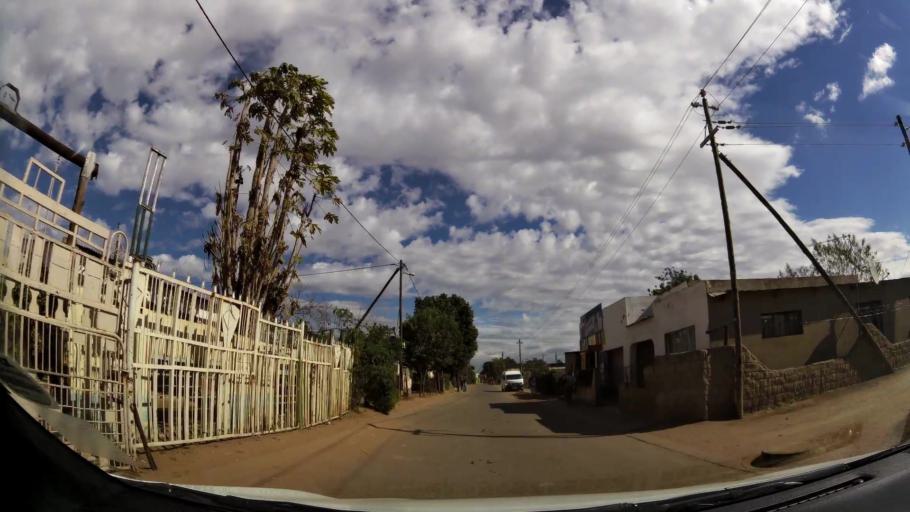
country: ZA
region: Limpopo
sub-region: Waterberg District Municipality
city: Bela-Bela
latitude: -24.8856
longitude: 28.3257
